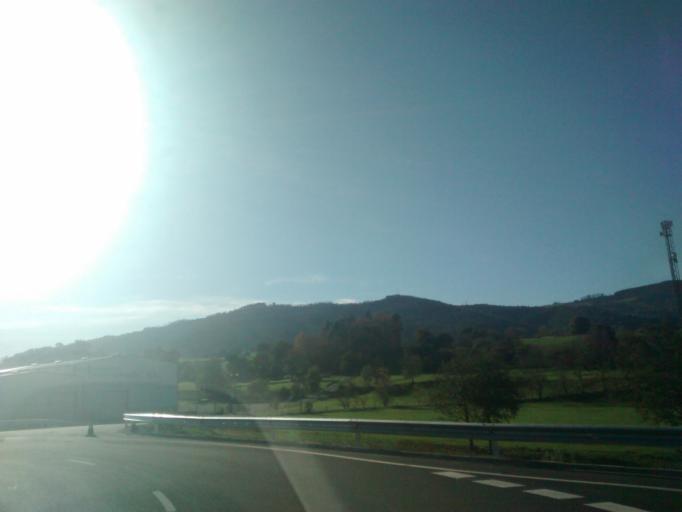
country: ES
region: Cantabria
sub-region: Provincia de Cantabria
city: Puente Viesgo
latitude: 43.3309
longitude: -3.9713
